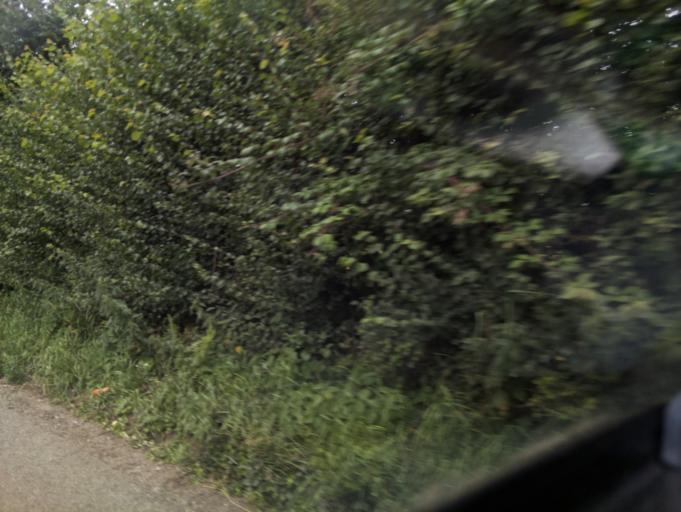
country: GB
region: England
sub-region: Somerset
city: Street
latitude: 51.1139
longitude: -2.7055
